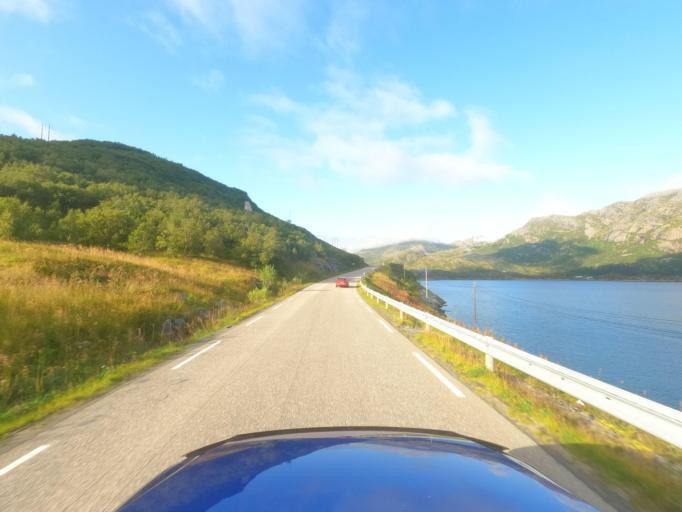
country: NO
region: Nordland
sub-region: Flakstad
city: Ramberg
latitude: 68.0112
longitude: 13.1675
